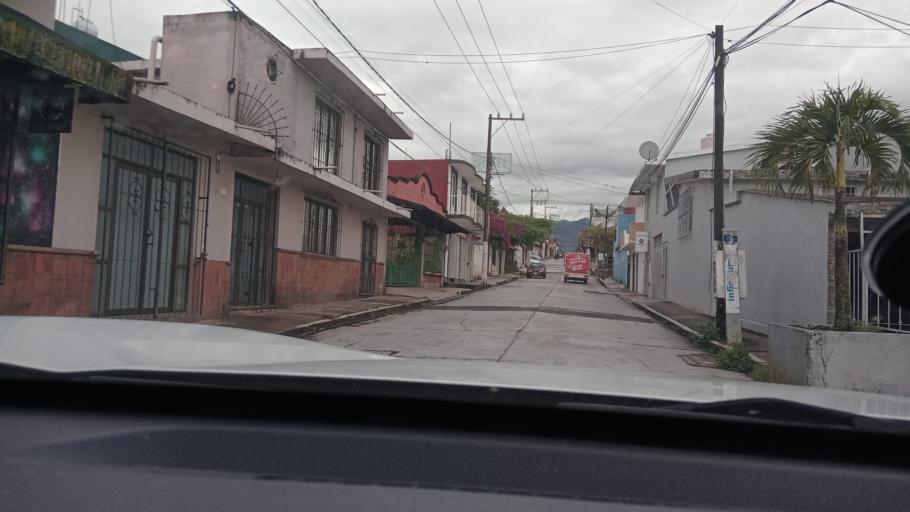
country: MX
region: Veracruz
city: Coatepec
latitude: 19.4480
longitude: -96.9555
